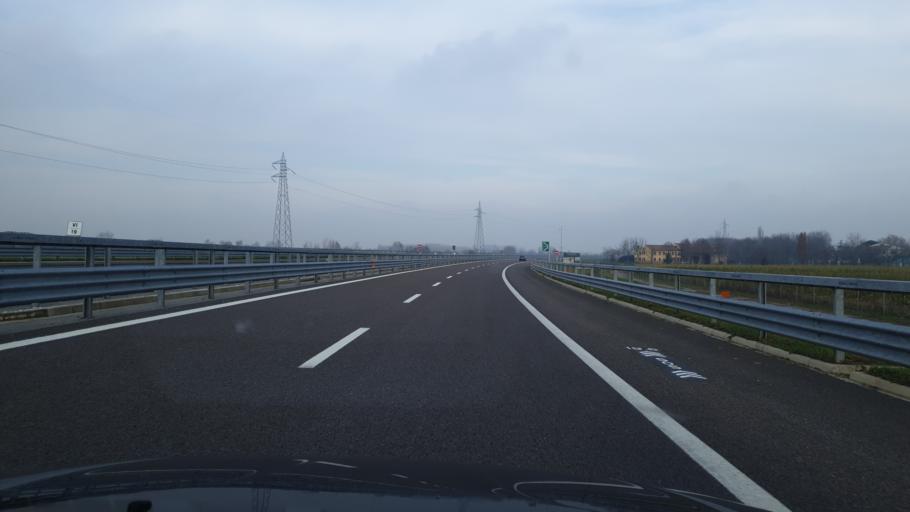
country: IT
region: Veneto
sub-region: Provincia di Padova
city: Saletto
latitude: 45.2296
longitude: 11.5515
